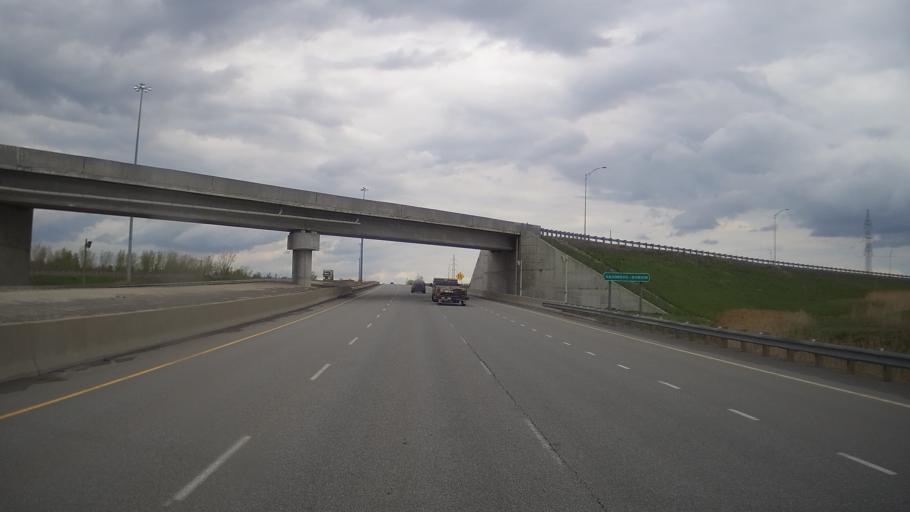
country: CA
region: Quebec
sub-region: Monteregie
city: Vaudreuil-Dorion
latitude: 45.3616
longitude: -74.0481
